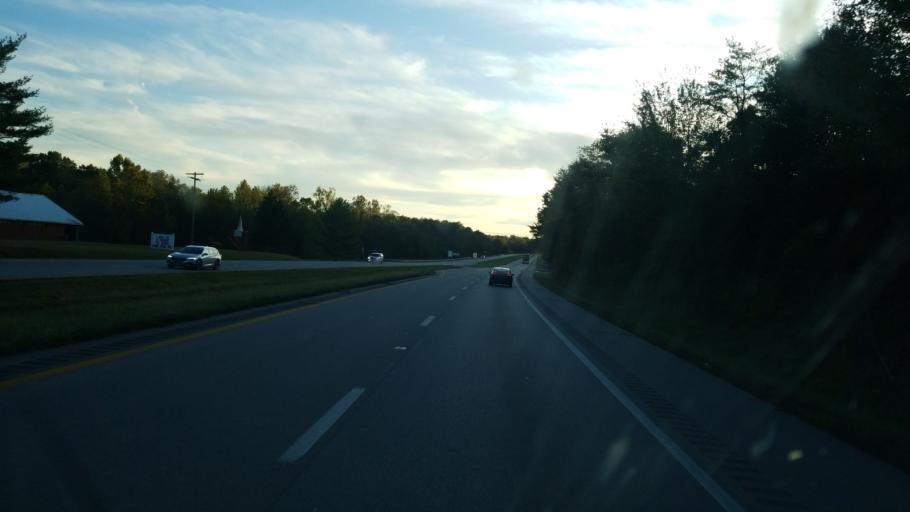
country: US
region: West Virginia
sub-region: Wood County
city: Washington
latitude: 39.2491
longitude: -81.7153
